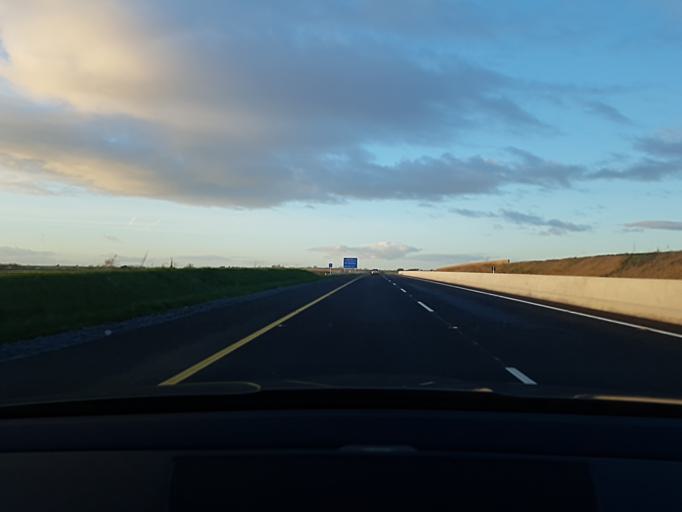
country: IE
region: Connaught
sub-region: County Galway
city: Athenry
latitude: 53.3820
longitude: -8.7988
